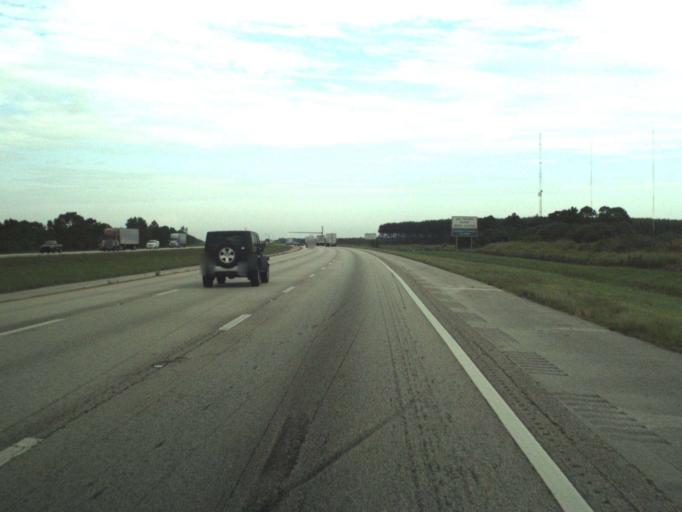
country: US
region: Florida
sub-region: Palm Beach County
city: Tequesta
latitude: 26.9902
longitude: -80.1902
